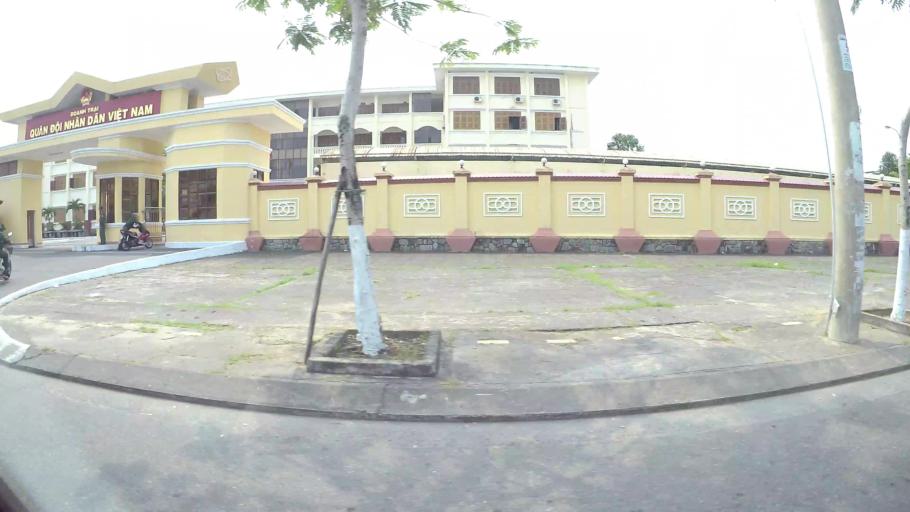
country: VN
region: Da Nang
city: Son Tra
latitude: 16.0485
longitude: 108.2209
